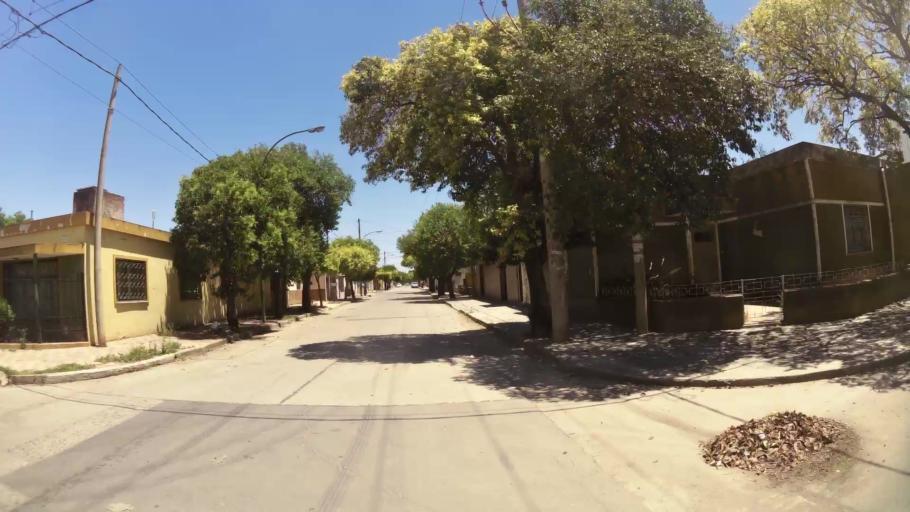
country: AR
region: Cordoba
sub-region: Departamento de Capital
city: Cordoba
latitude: -31.3784
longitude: -64.1326
